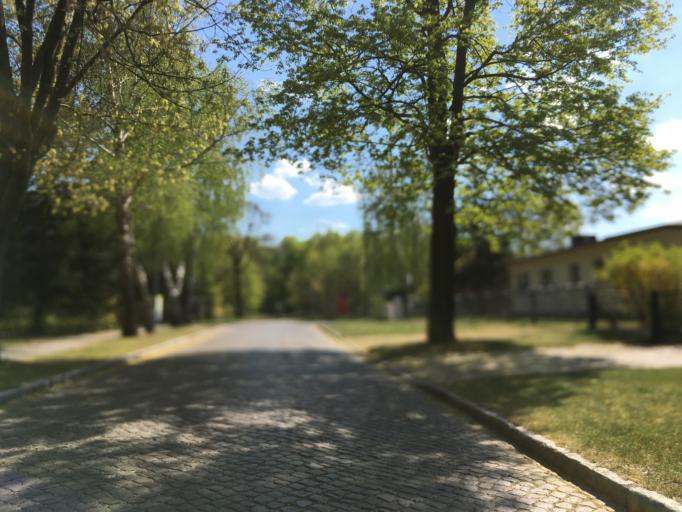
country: DE
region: Brandenburg
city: Werneuchen
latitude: 52.6194
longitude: 13.6767
